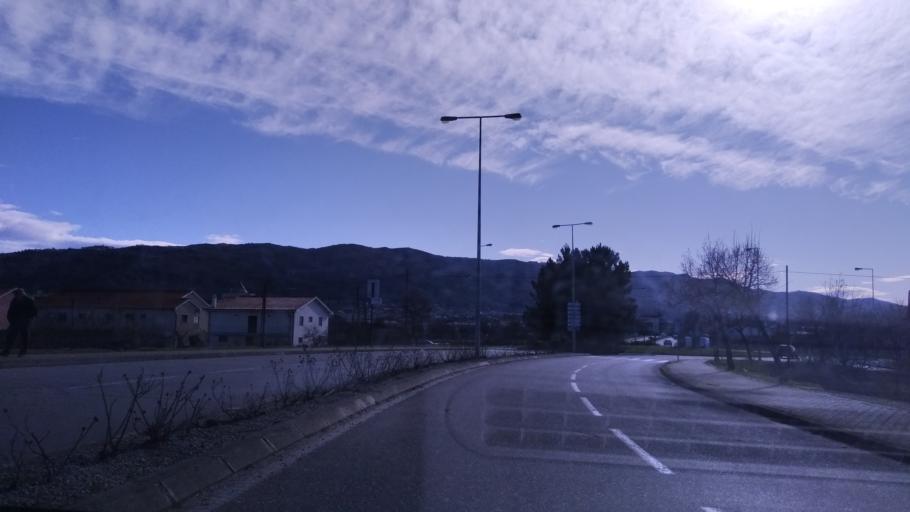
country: PT
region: Vila Real
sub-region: Chaves
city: Chaves
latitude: 41.7395
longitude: -7.4603
